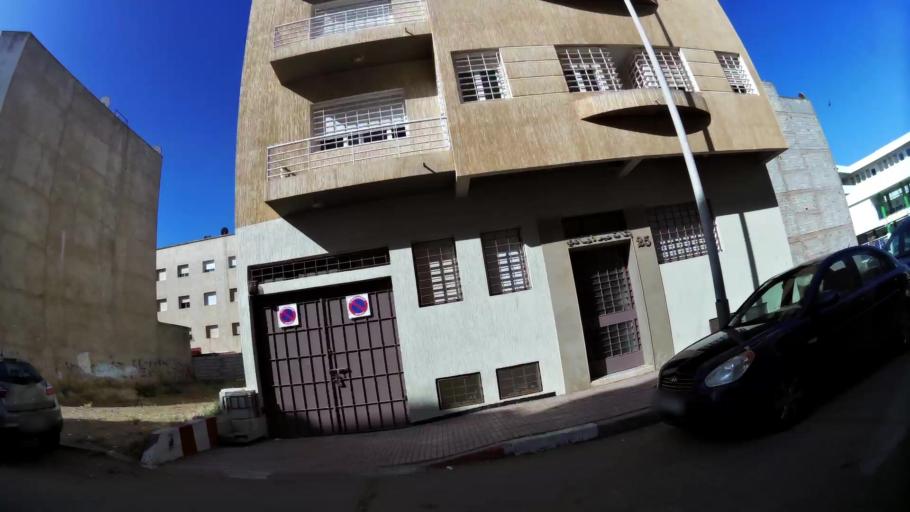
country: MA
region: Rabat-Sale-Zemmour-Zaer
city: Sale
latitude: 34.0615
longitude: -6.8062
